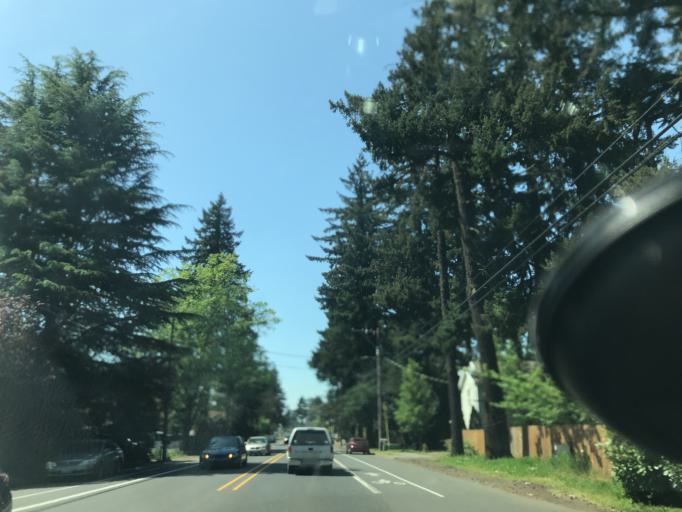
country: US
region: Oregon
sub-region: Multnomah County
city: Lents
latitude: 45.4970
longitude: -122.5409
